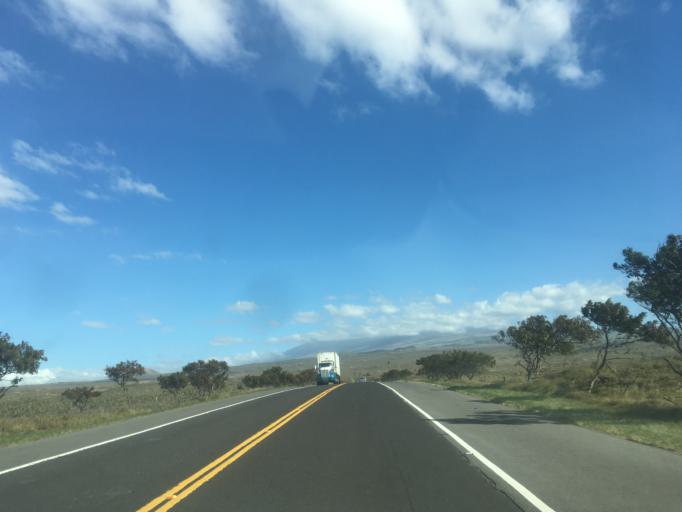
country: US
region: Hawaii
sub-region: Hawaii County
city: Waikoloa
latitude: 19.9064
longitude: -155.7659
